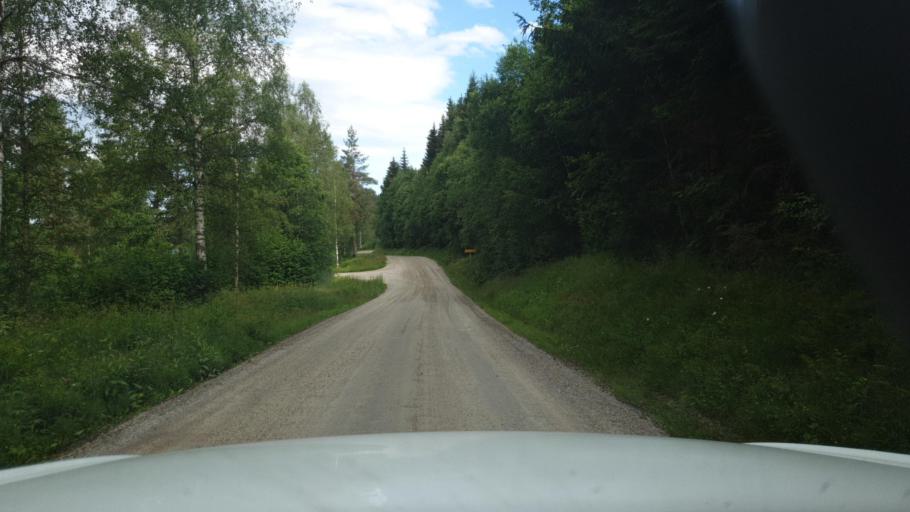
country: SE
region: Vaermland
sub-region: Arvika Kommun
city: Arvika
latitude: 59.7069
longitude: 12.8545
